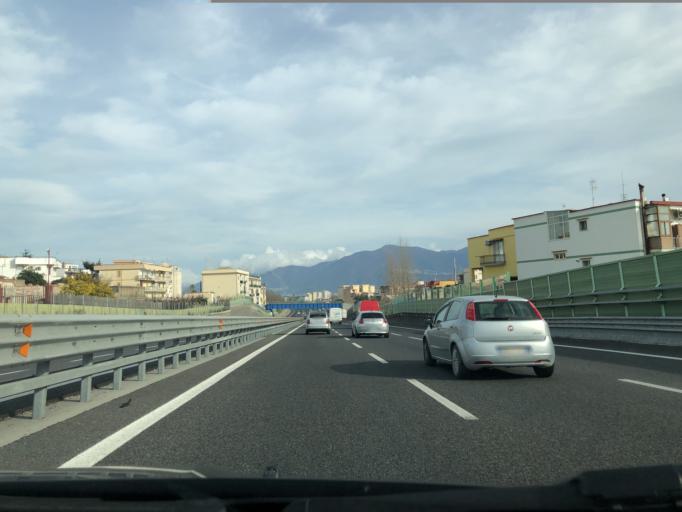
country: IT
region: Campania
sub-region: Provincia di Napoli
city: Trecase
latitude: 40.7639
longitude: 14.4371
